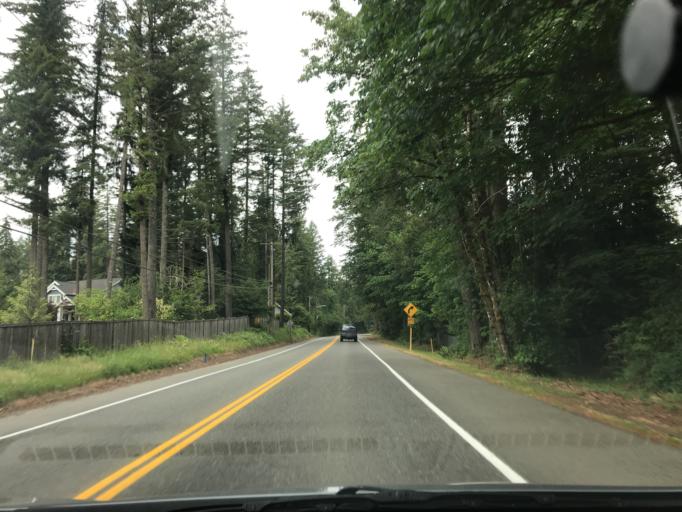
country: US
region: Washington
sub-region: King County
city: Black Diamond
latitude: 47.3089
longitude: -122.0460
